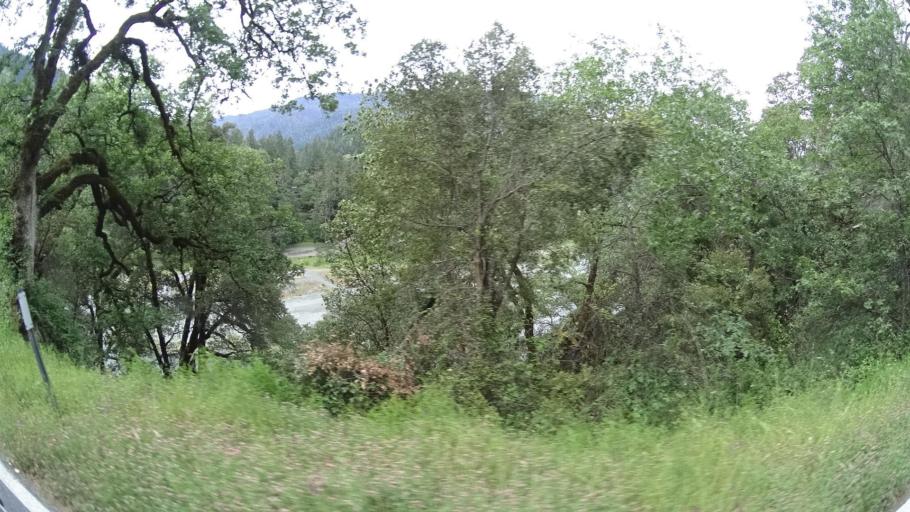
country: US
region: California
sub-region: Humboldt County
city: Willow Creek
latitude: 40.9496
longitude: -123.6135
